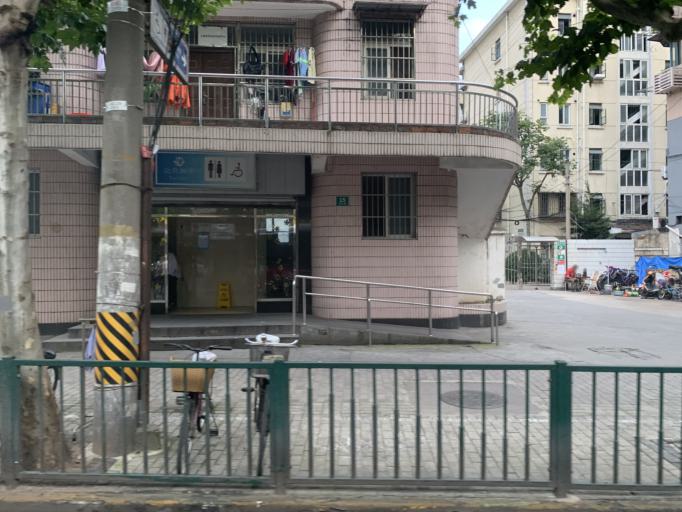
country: CN
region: Shanghai Shi
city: Pudong
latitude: 31.2479
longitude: 121.5531
